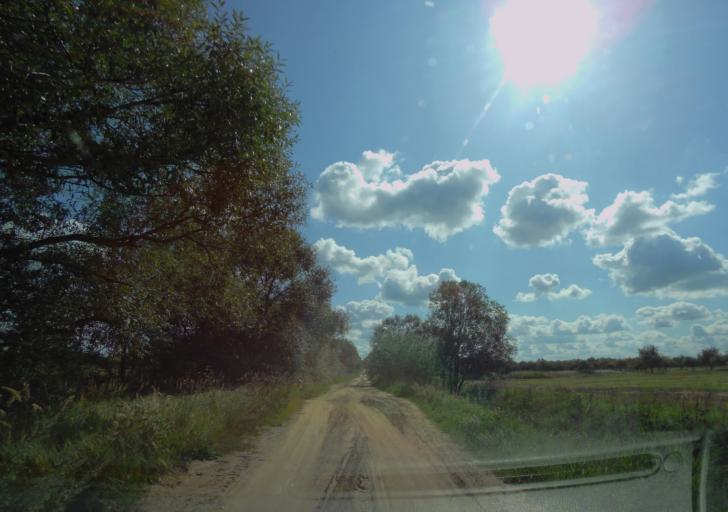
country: BY
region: Minsk
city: Zyembin
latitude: 54.4138
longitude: 28.3759
